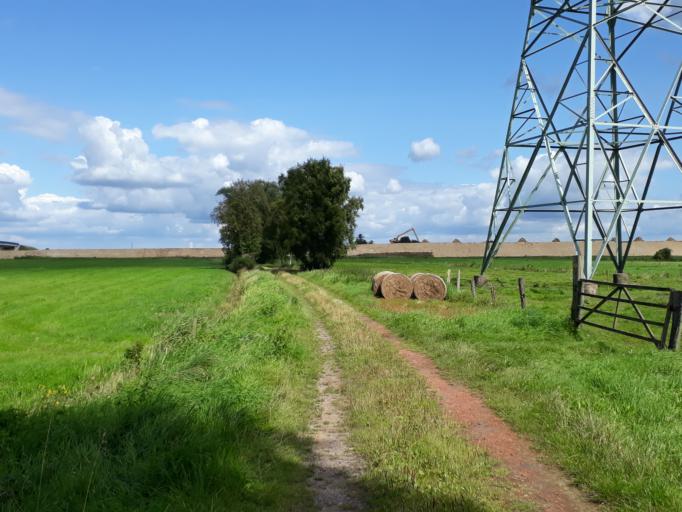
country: DE
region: Lower Saxony
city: Buxtehude
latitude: 53.4931
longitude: 9.6796
